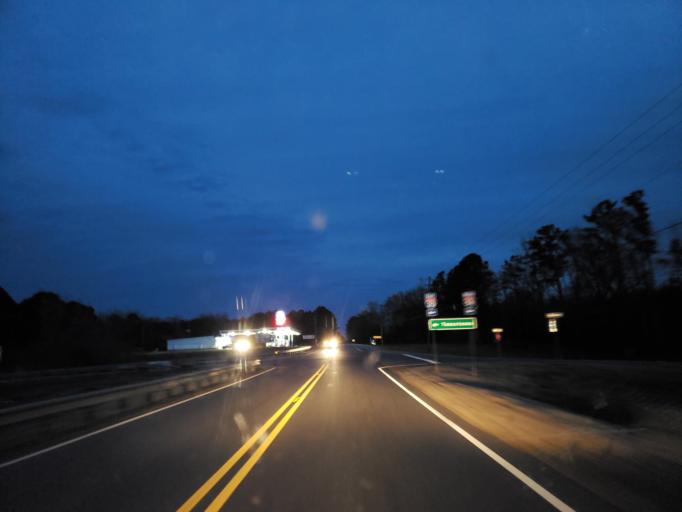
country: US
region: Alabama
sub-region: Greene County
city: Eutaw
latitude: 32.8684
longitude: -87.9235
